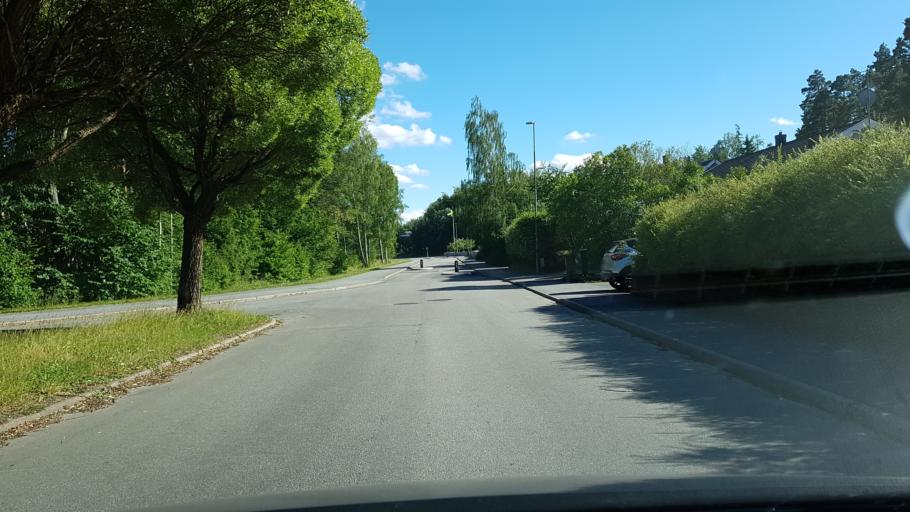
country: SE
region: Stockholm
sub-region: Upplands-Bro Kommun
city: Kungsaengen
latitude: 59.4769
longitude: 17.8043
